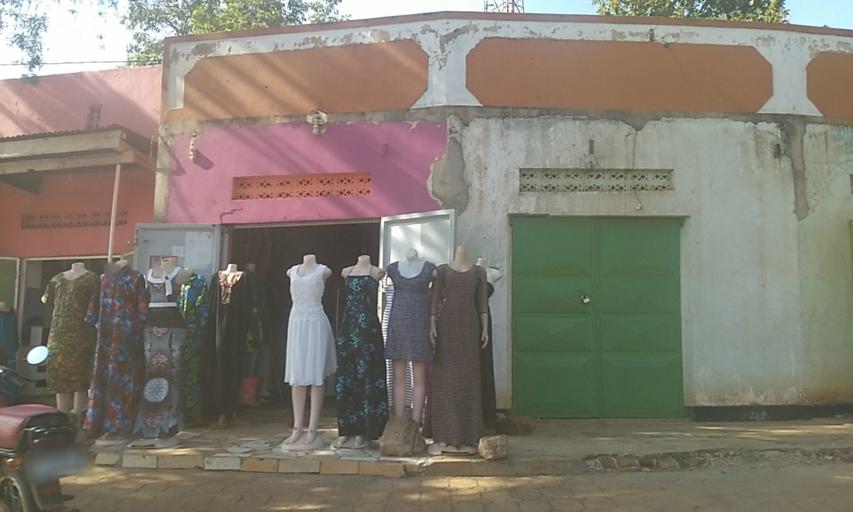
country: UG
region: Central Region
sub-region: Wakiso District
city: Kireka
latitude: 0.3631
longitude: 32.6256
